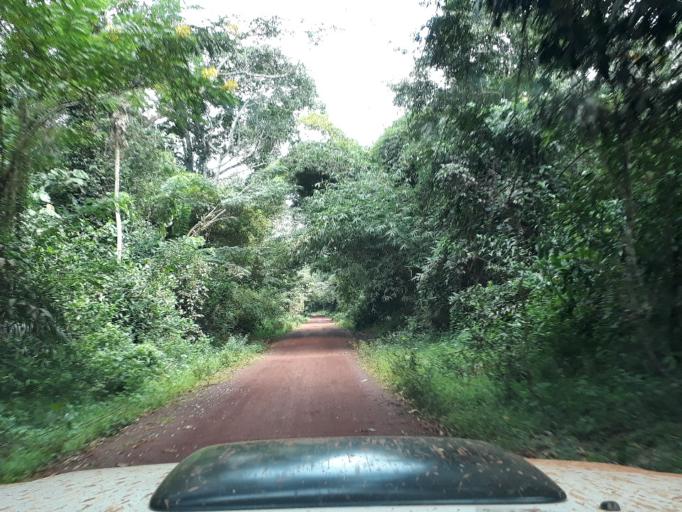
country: CD
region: Eastern Province
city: Buta
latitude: 2.2886
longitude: 25.0535
